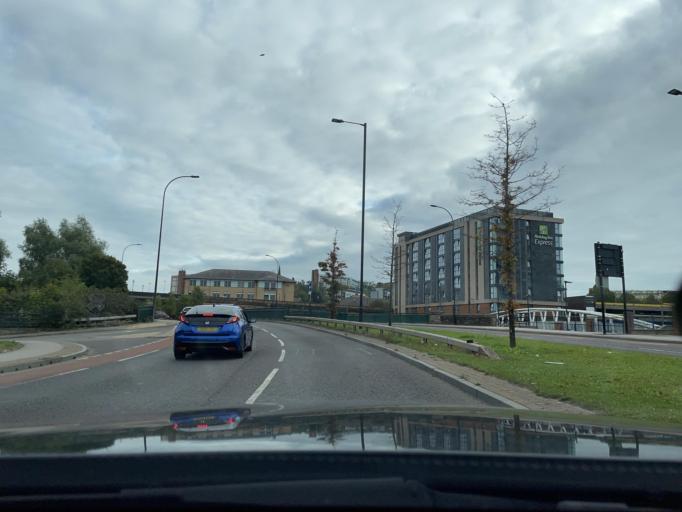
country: GB
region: England
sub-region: Sheffield
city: Sheffield
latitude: 53.3872
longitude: -1.4616
